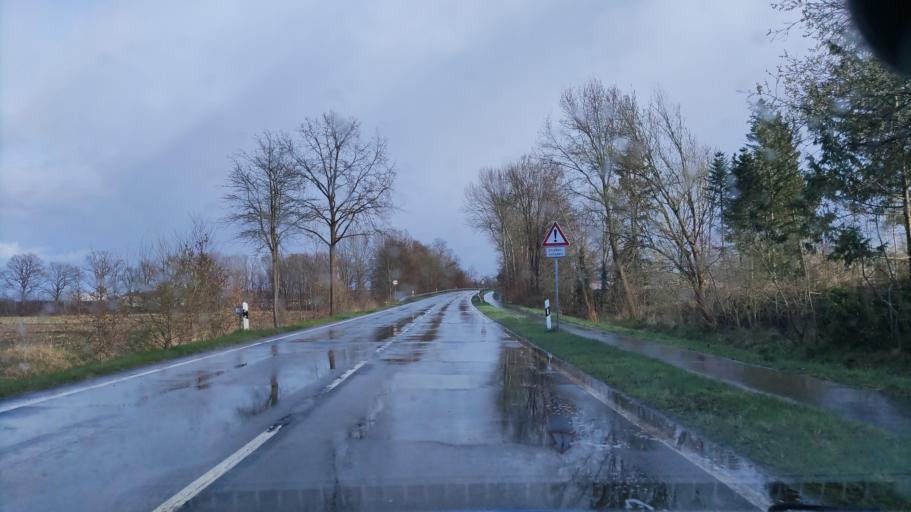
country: DE
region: Lower Saxony
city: Eschede
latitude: 52.7447
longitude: 10.2297
